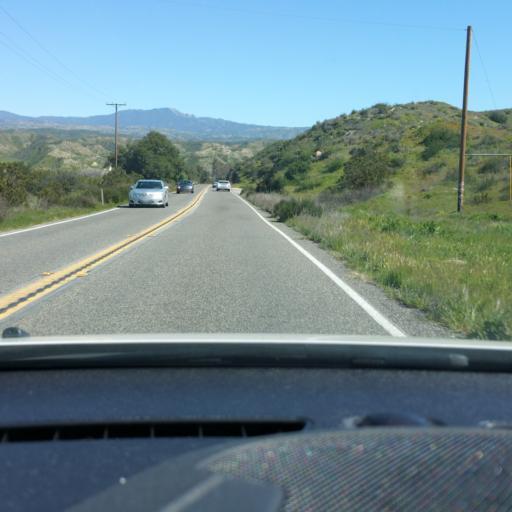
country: US
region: California
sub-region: Riverside County
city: Aguanga
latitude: 33.4672
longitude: -116.9594
